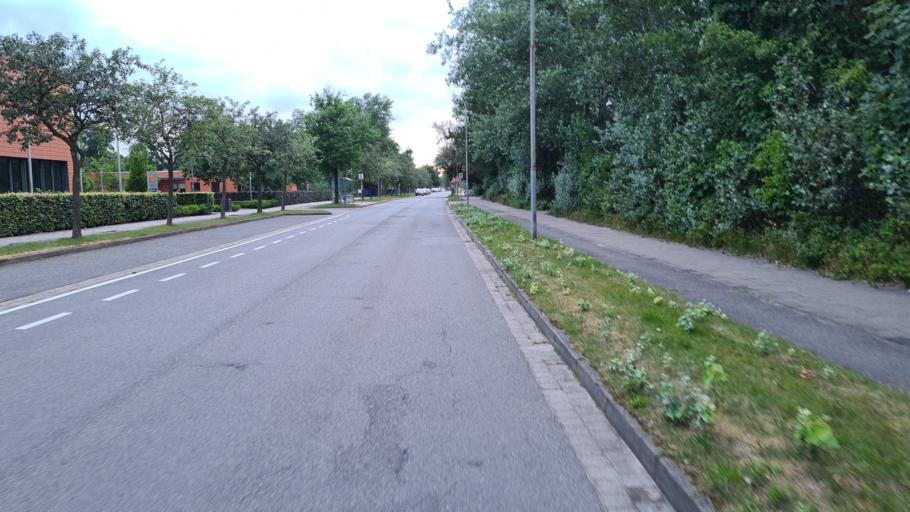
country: DE
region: Schleswig-Holstein
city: Sankt Peter-Ording
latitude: 54.2942
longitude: 8.6500
